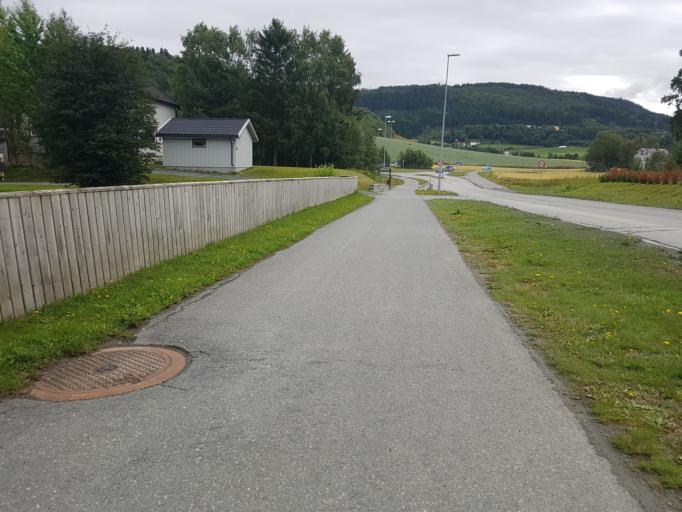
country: NO
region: Sor-Trondelag
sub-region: Trondheim
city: Trondheim
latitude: 63.3835
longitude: 10.4323
